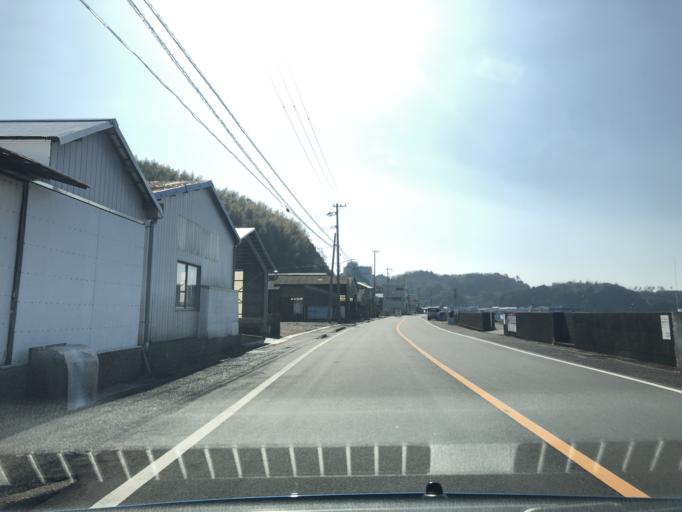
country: JP
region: Kochi
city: Sukumo
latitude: 32.9244
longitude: 132.6956
